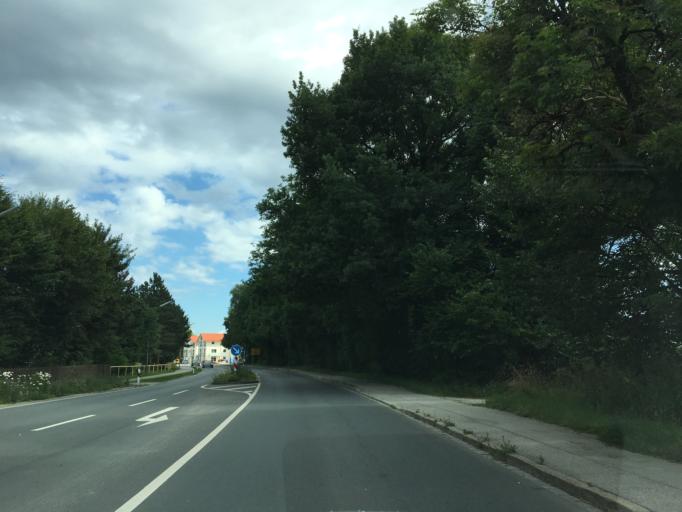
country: DE
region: Bavaria
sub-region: Upper Bavaria
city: Otterfing
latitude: 47.9056
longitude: 11.6764
